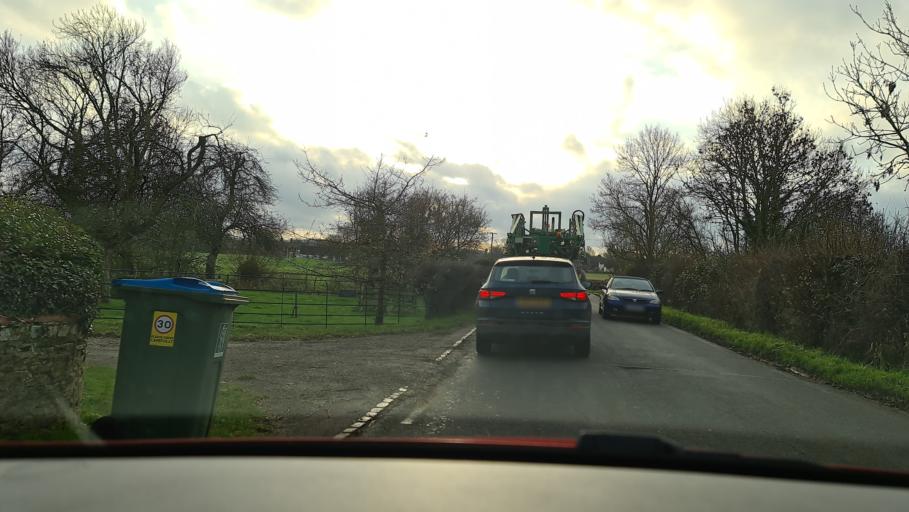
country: GB
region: England
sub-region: Buckinghamshire
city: Stone
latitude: 51.7799
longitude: -0.8770
